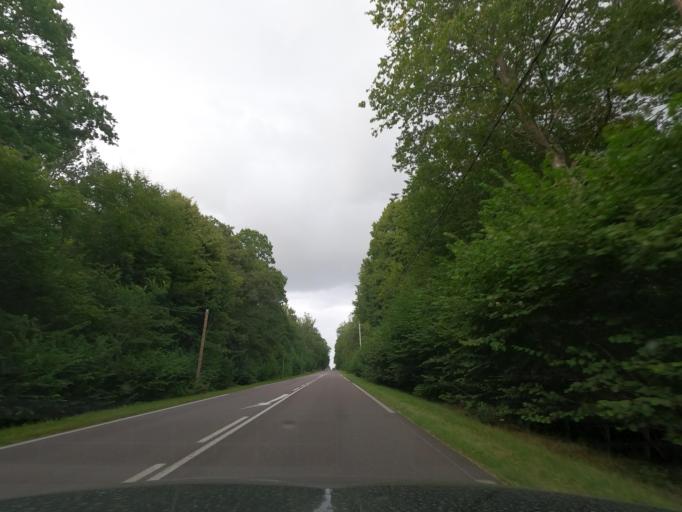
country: FR
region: Haute-Normandie
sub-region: Departement de l'Eure
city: Menneval
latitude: 49.1227
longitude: 0.6314
